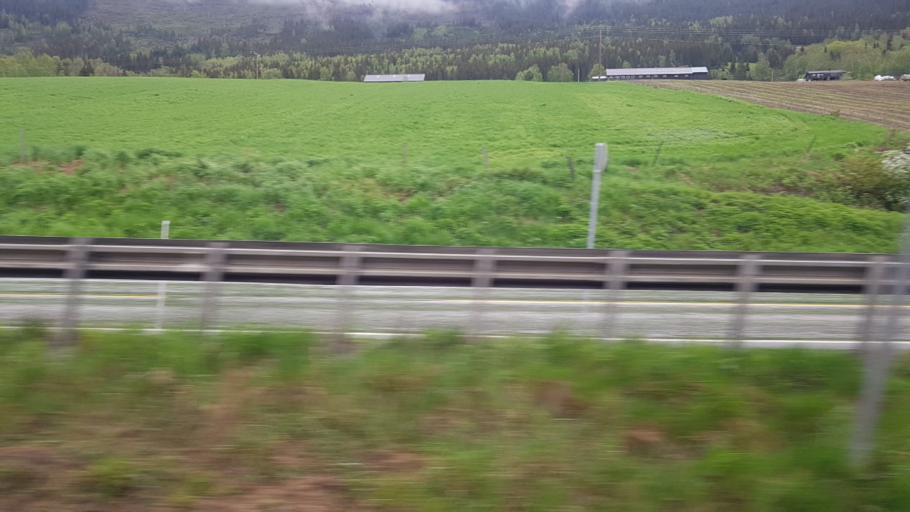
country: NO
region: Oppland
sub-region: Nord-Fron
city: Vinstra
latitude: 61.6227
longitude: 9.7147
